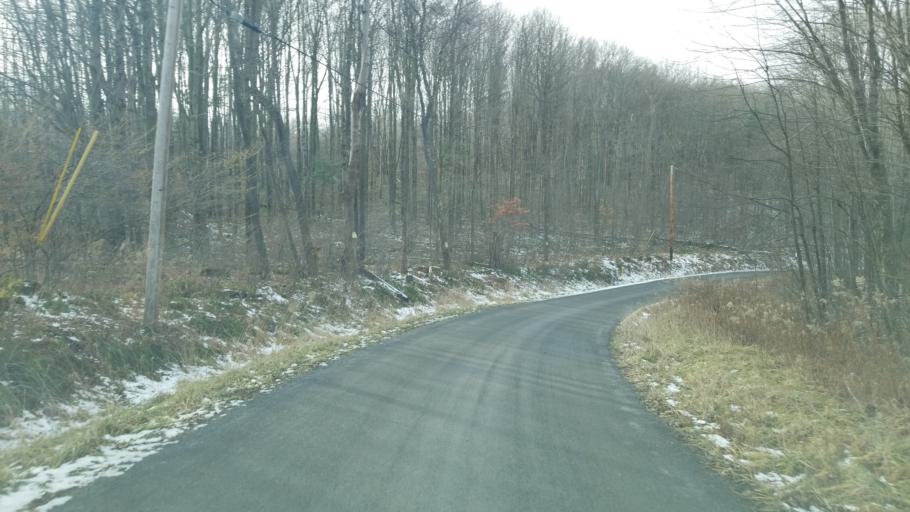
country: US
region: Pennsylvania
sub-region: Jefferson County
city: Punxsutawney
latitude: 40.8672
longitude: -79.0329
